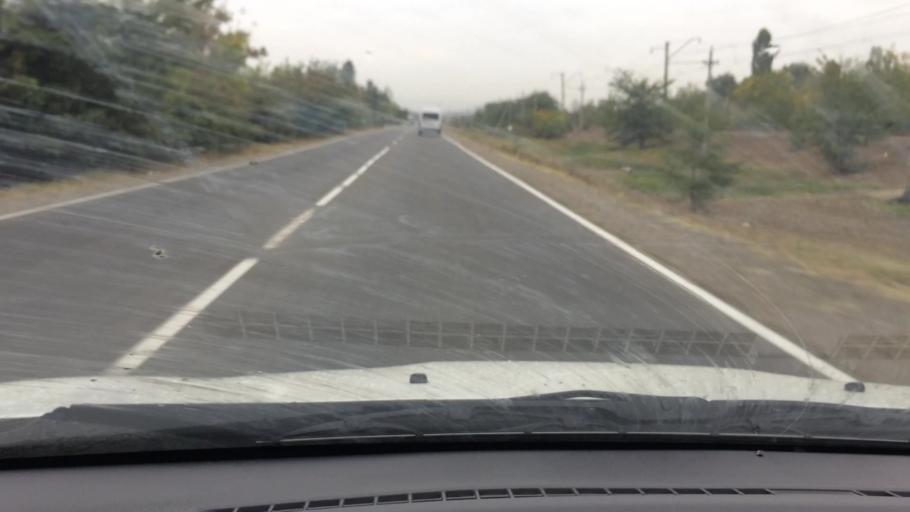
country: GE
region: Kvemo Kartli
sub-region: Marneuli
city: Marneuli
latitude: 41.4521
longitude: 44.8132
